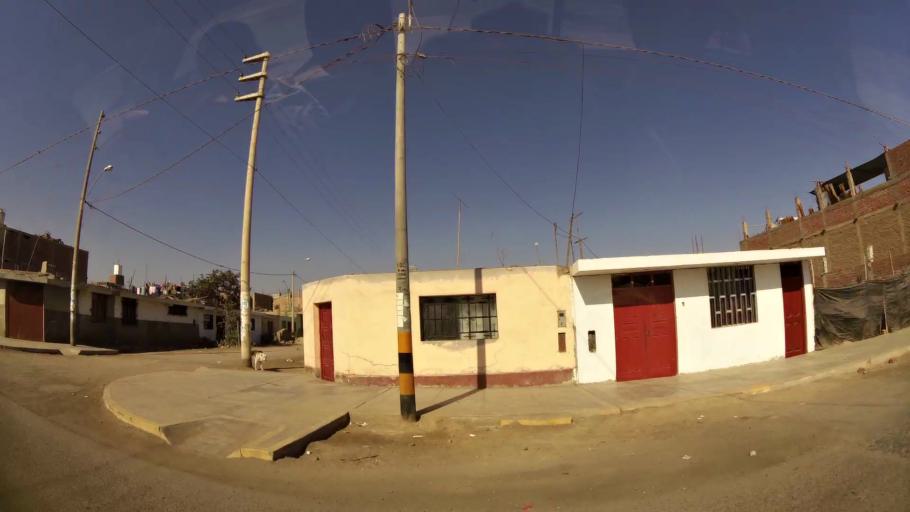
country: PE
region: Ica
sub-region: Provincia de Chincha
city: Chincha Alta
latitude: -13.4027
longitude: -76.1243
